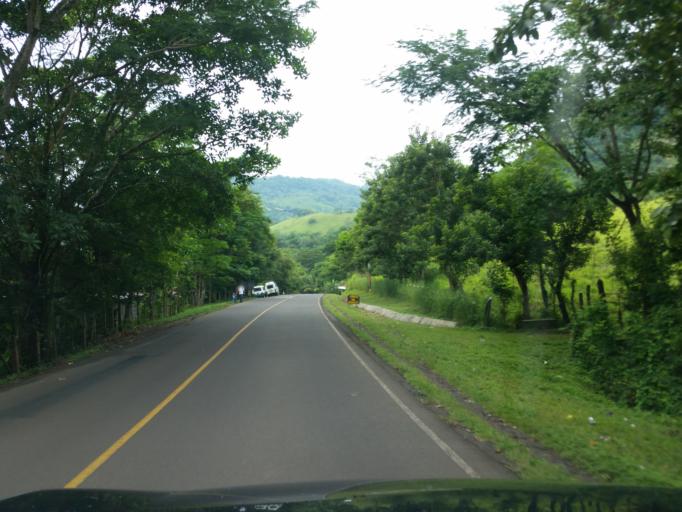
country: NI
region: Matagalpa
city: San Ramon
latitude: 13.0521
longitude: -85.7593
